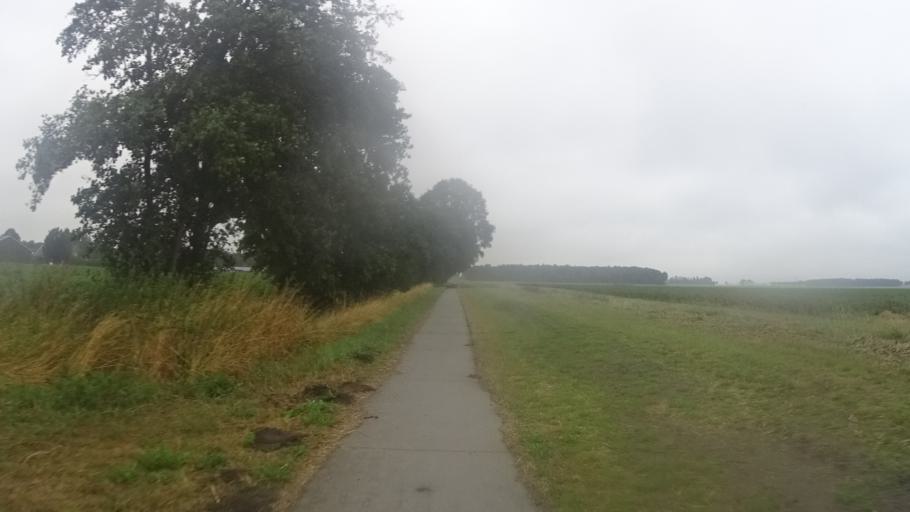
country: NL
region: Groningen
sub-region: Gemeente Veendam
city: Veendam
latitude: 53.1816
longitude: 6.8789
